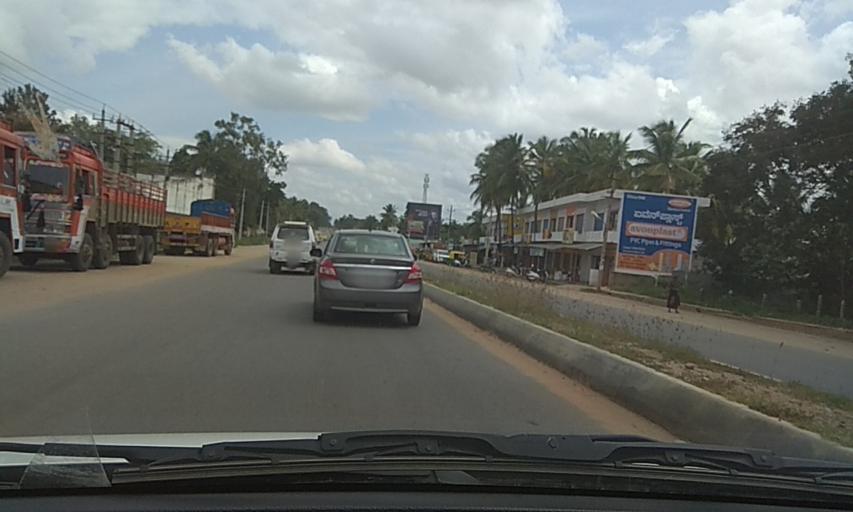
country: IN
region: Karnataka
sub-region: Tumkur
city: Tumkur
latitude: 13.3746
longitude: 77.0999
